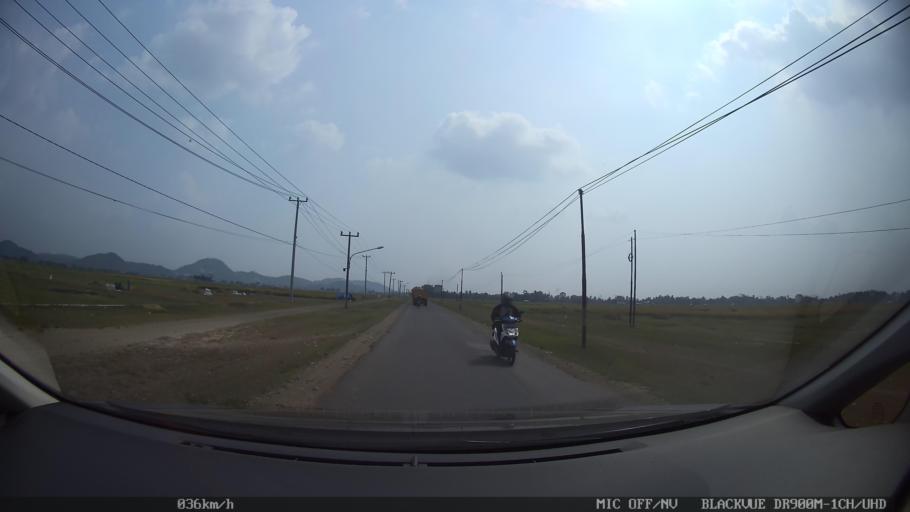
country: ID
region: Lampung
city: Pringsewu
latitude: -5.3553
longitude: 105.0123
